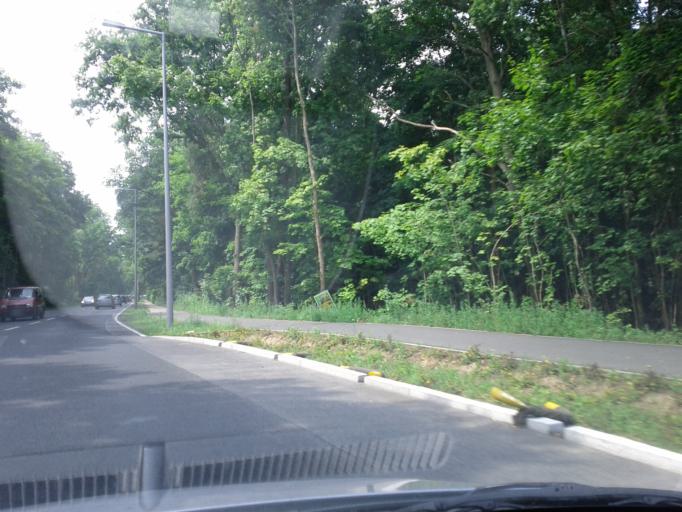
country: DE
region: Berlin
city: Adlershof
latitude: 52.4491
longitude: 13.5481
